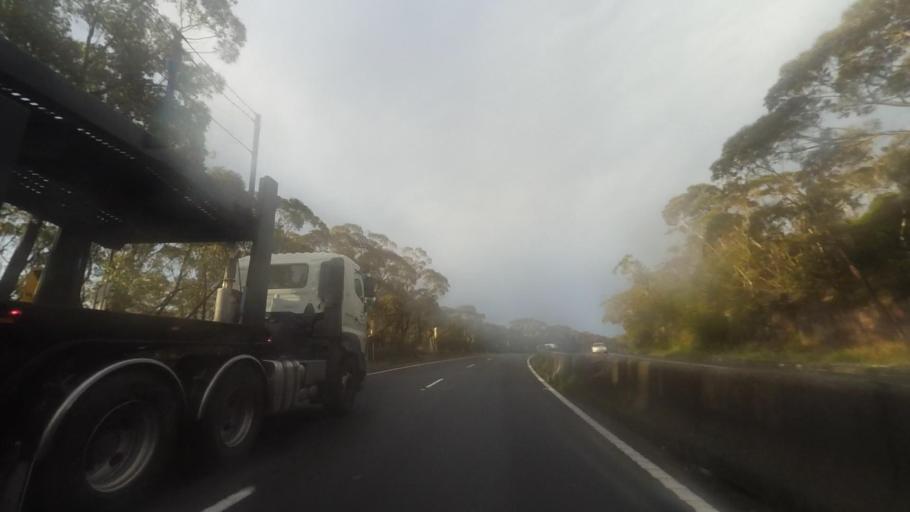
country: AU
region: New South Wales
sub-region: Wollongong
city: Mount Ousley
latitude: -34.3569
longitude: 150.8573
